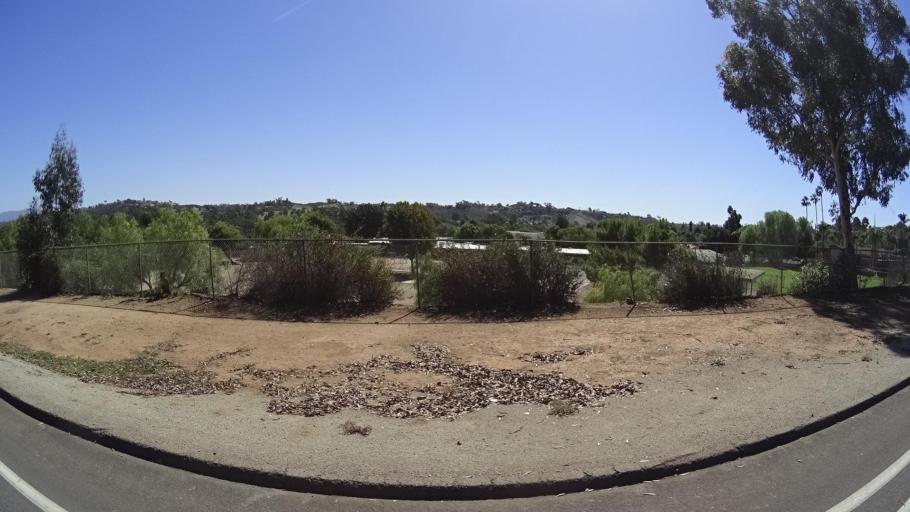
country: US
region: California
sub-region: San Diego County
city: Bonita
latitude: 32.6610
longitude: -117.0484
